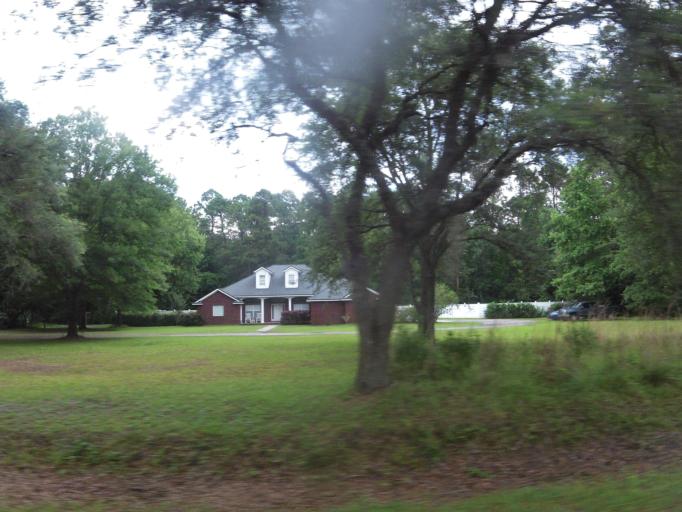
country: US
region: Florida
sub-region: Duval County
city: Baldwin
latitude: 30.3389
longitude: -81.8761
